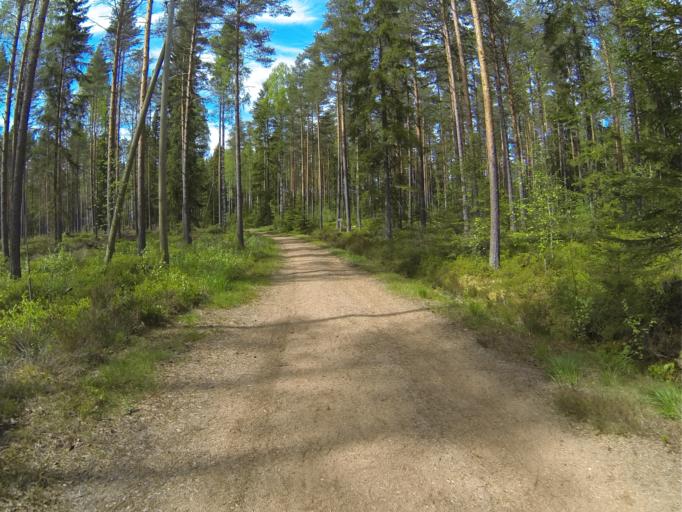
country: FI
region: Varsinais-Suomi
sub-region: Salo
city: Salo
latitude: 60.3847
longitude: 23.1971
